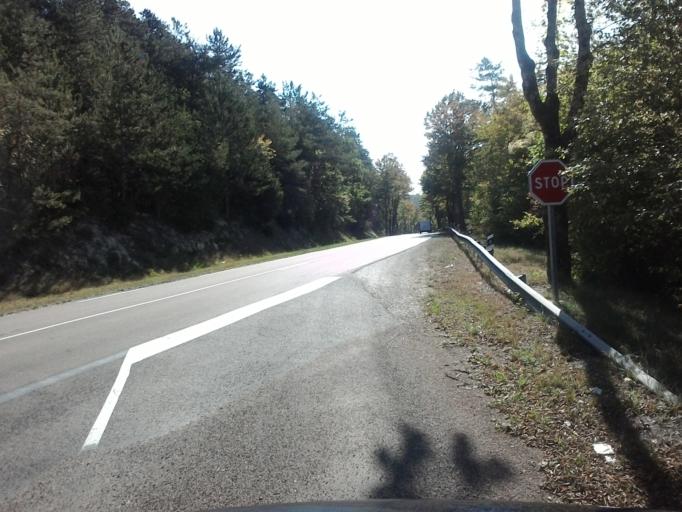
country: FR
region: Champagne-Ardenne
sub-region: Departement de l'Aube
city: Mussy-sur-Seine
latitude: 48.0005
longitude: 4.4752
